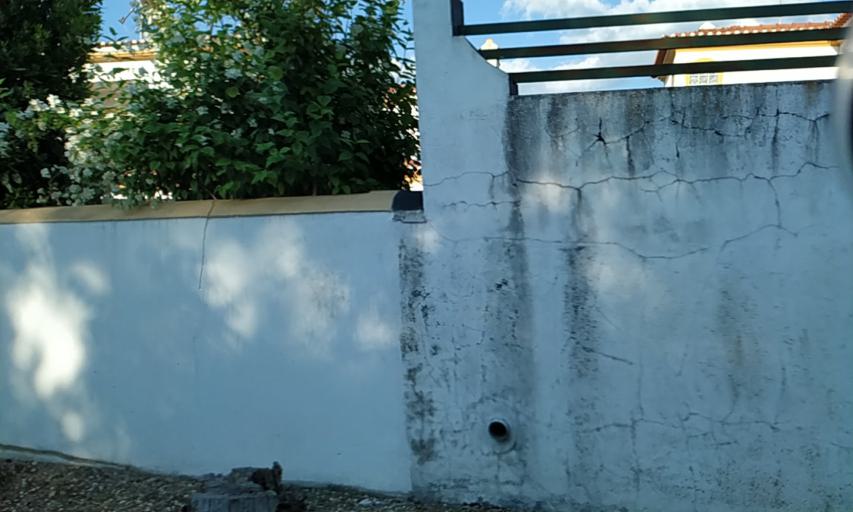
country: PT
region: Portalegre
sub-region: Portalegre
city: Portalegre
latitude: 39.3130
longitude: -7.4415
